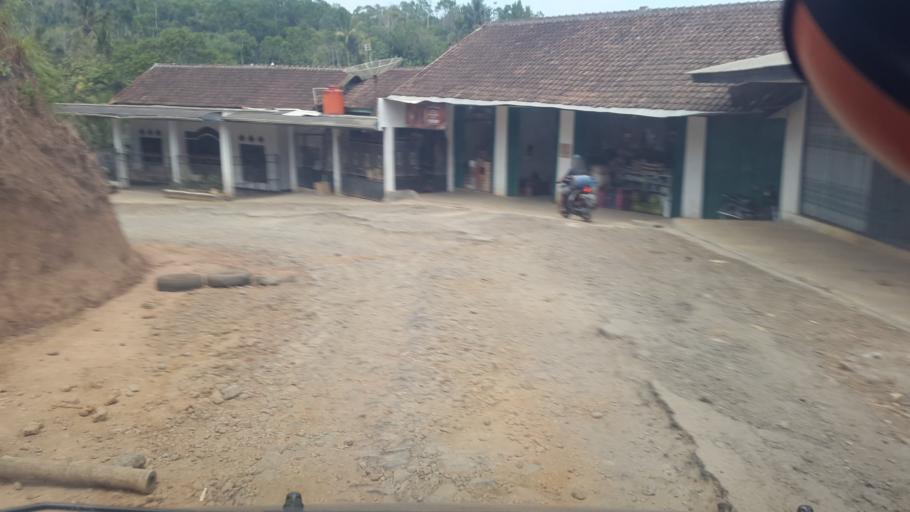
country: ID
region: West Java
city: Cisireum
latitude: -7.1159
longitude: 106.6421
